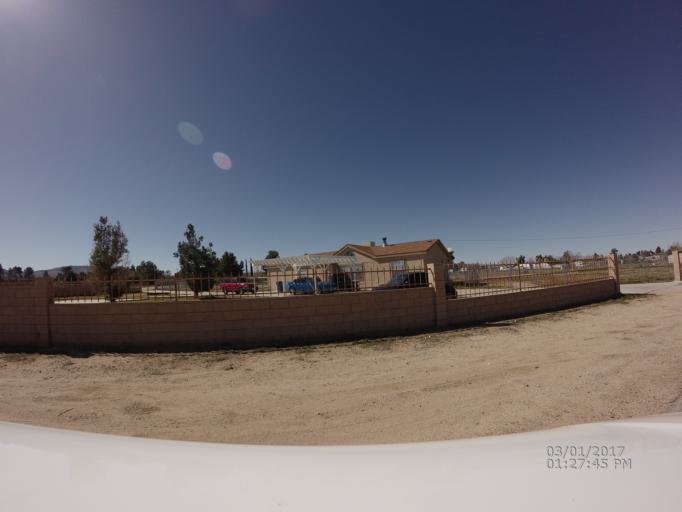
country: US
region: California
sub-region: Los Angeles County
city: Desert View Highlands
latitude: 34.6168
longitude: -118.1566
